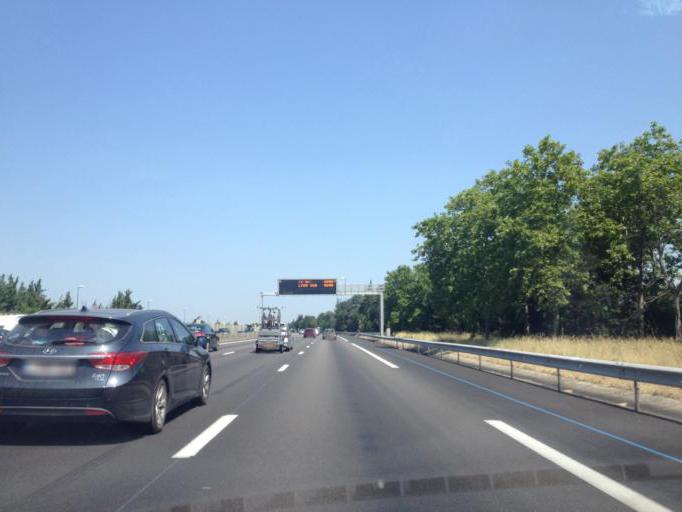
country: FR
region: Rhone-Alpes
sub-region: Departement de la Drome
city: Bourg-les-Valence
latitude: 44.9541
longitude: 4.8884
